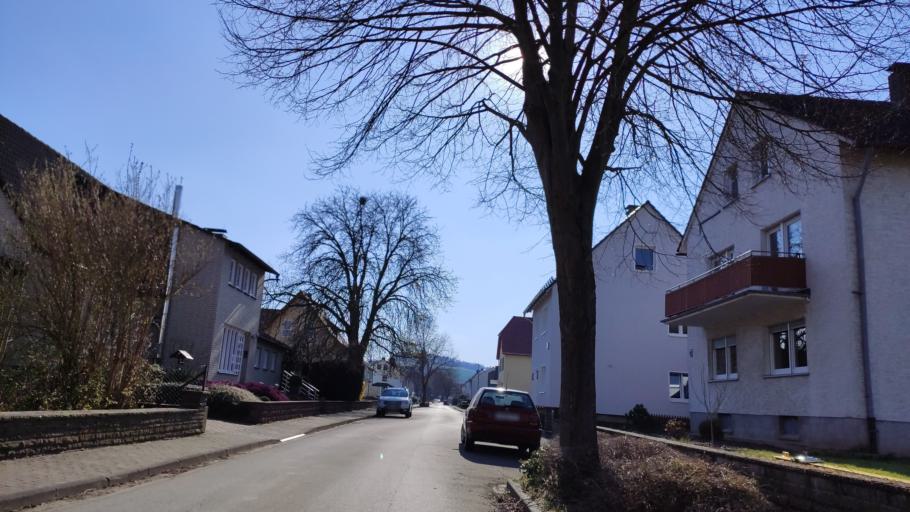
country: DE
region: Lower Saxony
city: Boffzen
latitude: 51.7148
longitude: 9.3475
